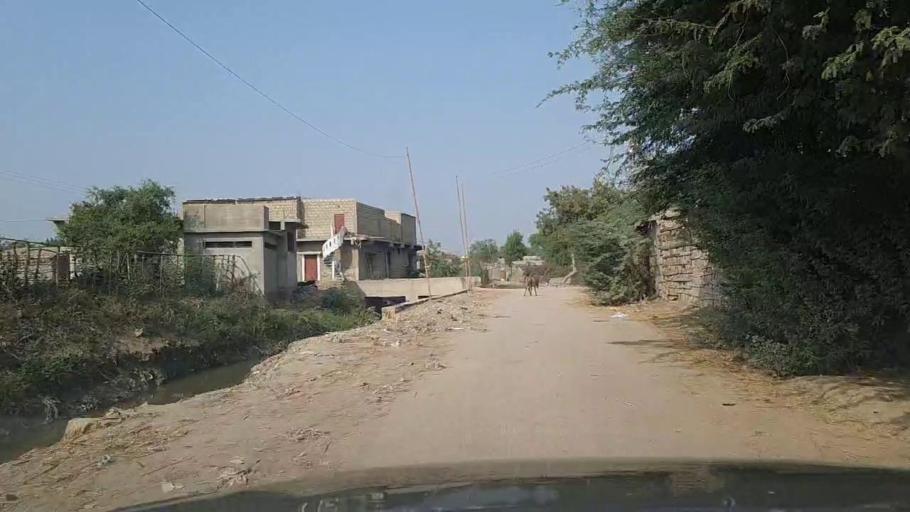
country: PK
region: Sindh
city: Mirpur Batoro
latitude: 24.7243
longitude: 68.2570
